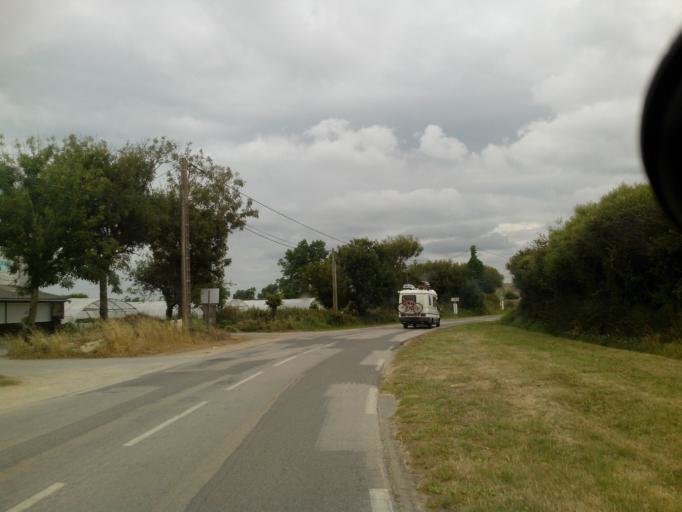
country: FR
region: Brittany
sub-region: Departement du Morbihan
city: Erdeven
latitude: 47.6198
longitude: -3.1658
